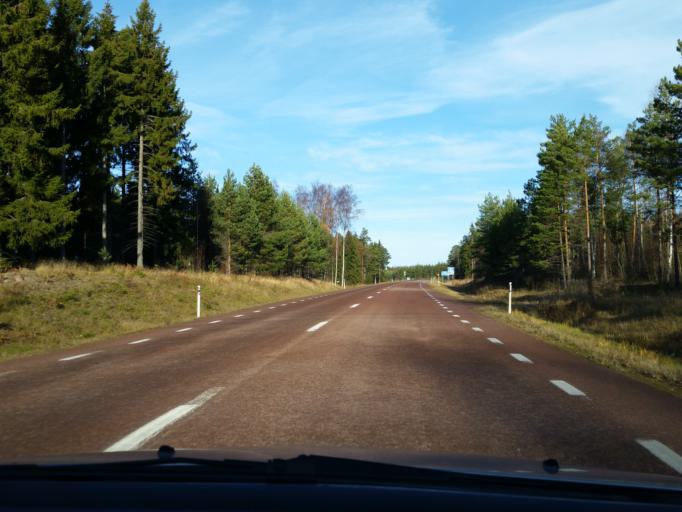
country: AX
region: Alands landsbygd
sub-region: Finstroem
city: Finstroem
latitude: 60.3003
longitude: 19.9526
